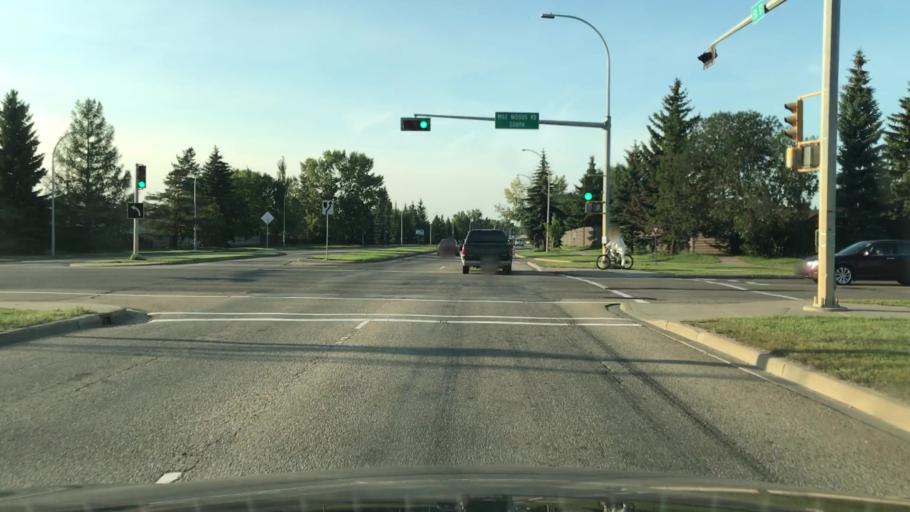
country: CA
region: Alberta
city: Beaumont
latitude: 53.4455
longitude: -113.4192
